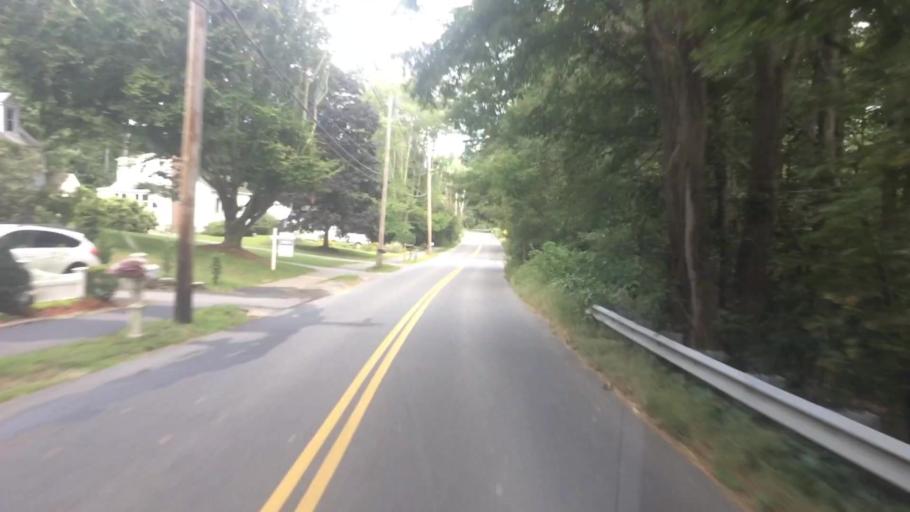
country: US
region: Massachusetts
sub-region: Middlesex County
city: West Concord
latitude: 42.4615
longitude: -71.4191
